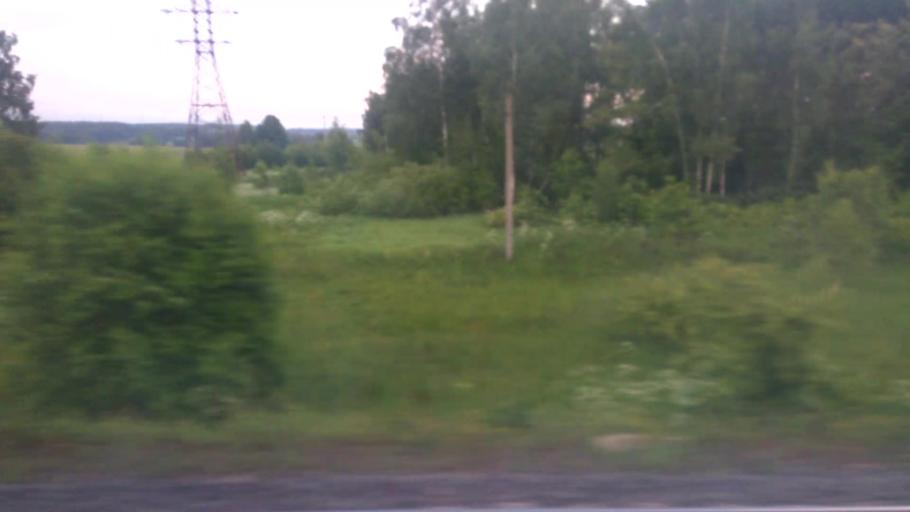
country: RU
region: Moskovskaya
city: Mikhnevo
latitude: 55.0812
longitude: 37.9751
